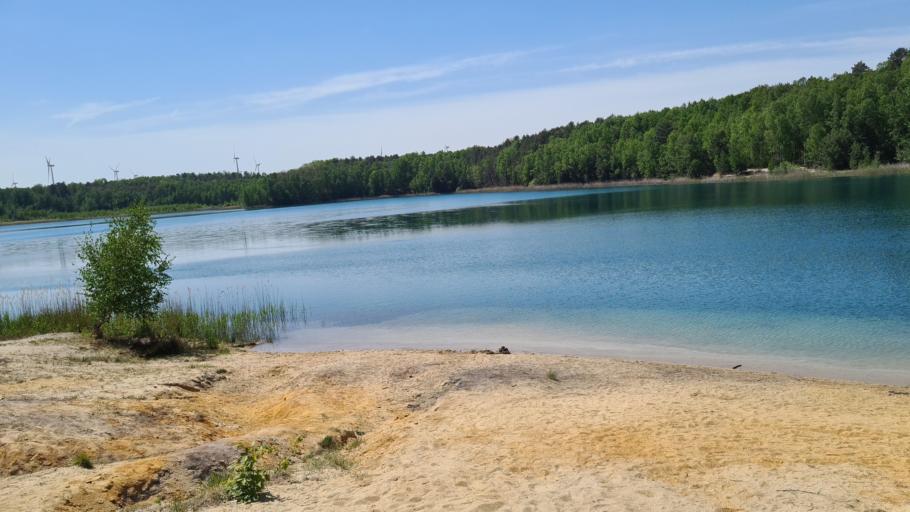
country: DE
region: Brandenburg
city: Sallgast
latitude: 51.5752
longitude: 13.8426
